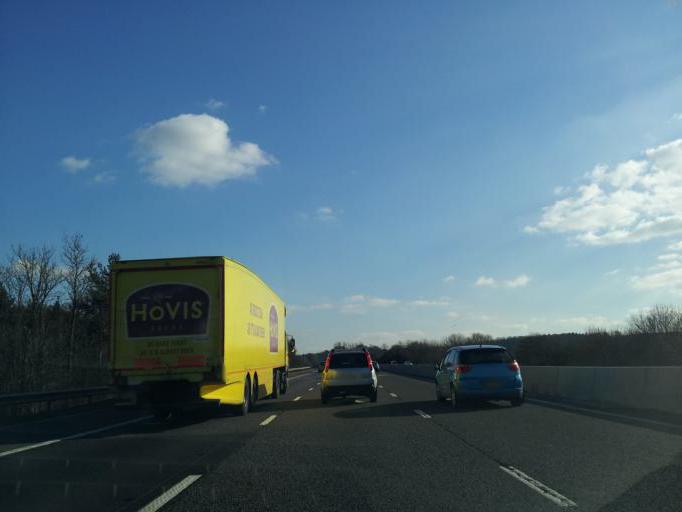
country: GB
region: England
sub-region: North Somerset
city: Banwell
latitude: 51.3288
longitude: -2.8926
